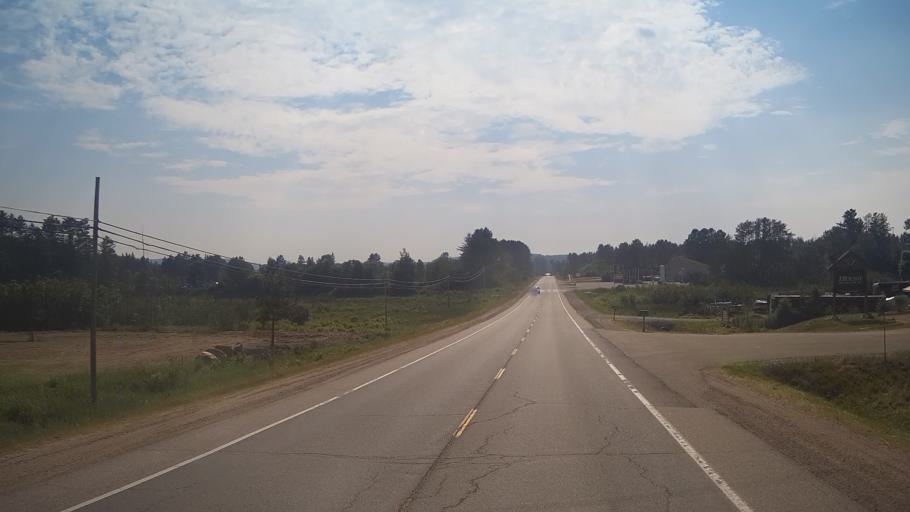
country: CA
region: Ontario
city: Bancroft
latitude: 45.4905
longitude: -77.6569
